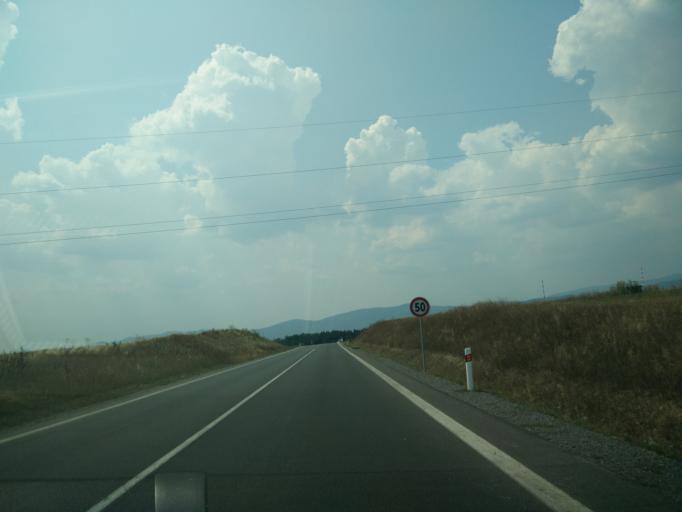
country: SK
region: Banskobystricky
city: Ziar nad Hronom
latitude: 48.5846
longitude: 18.8368
